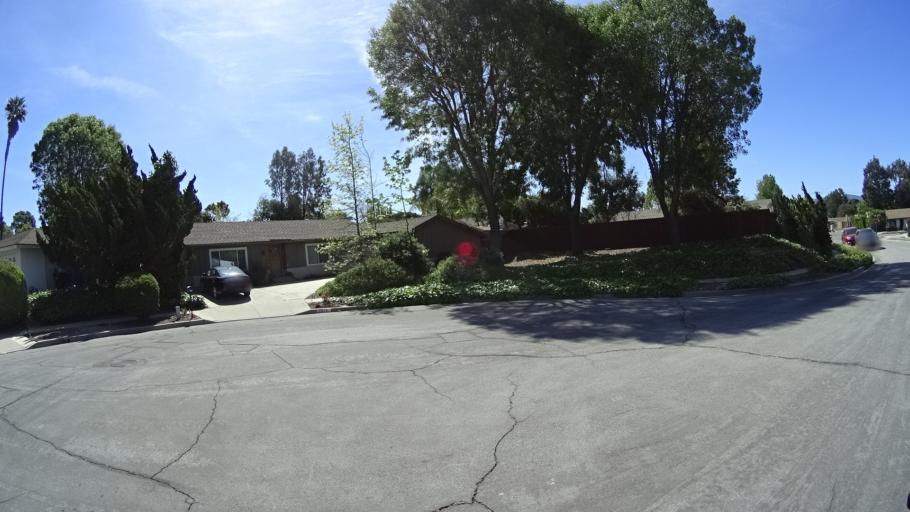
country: US
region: California
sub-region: Ventura County
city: Thousand Oaks
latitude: 34.2172
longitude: -118.8601
